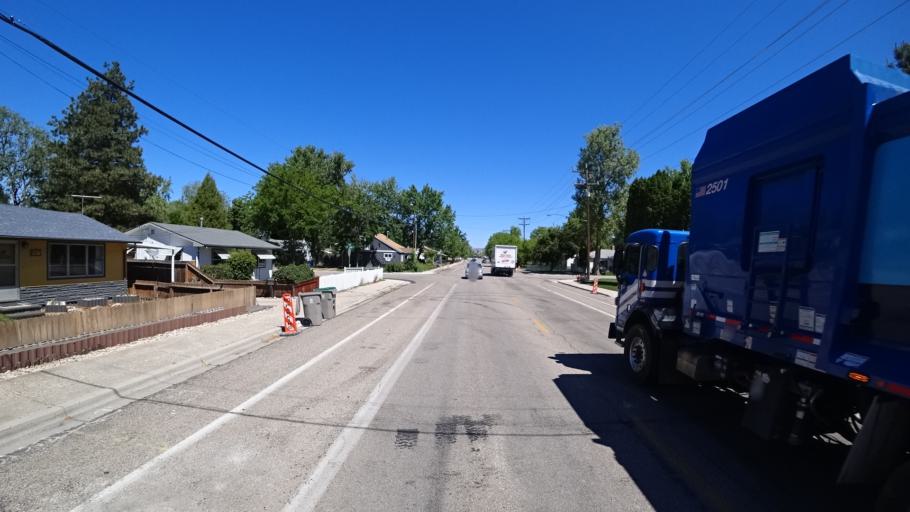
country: US
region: Idaho
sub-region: Ada County
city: Garden City
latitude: 43.5986
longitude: -116.2286
